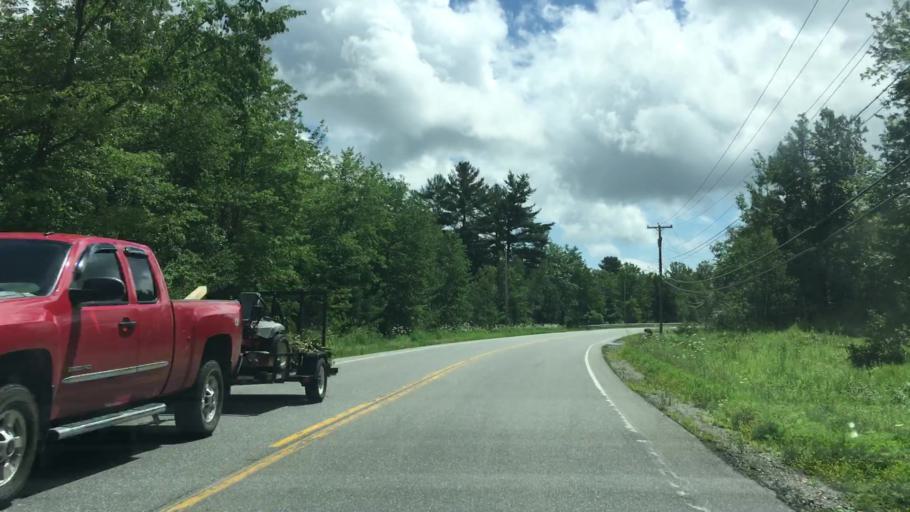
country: US
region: Maine
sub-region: Penobscot County
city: Hermon
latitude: 44.8077
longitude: -68.9710
